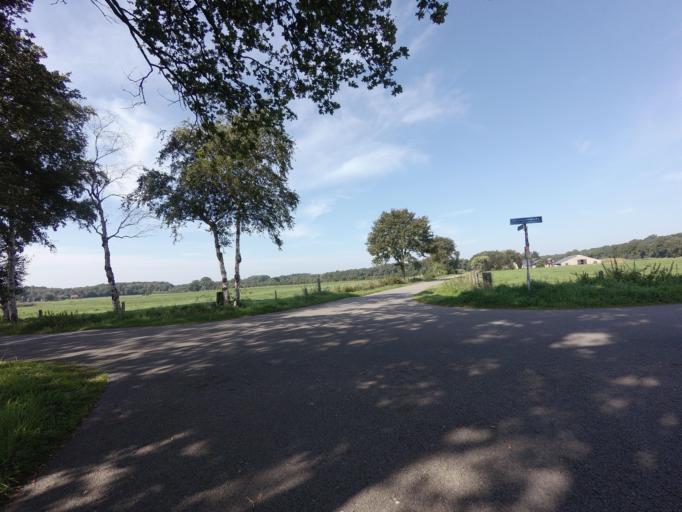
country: NL
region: Overijssel
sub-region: Gemeente Enschede
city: Enschede
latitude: 52.1866
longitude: 6.9189
